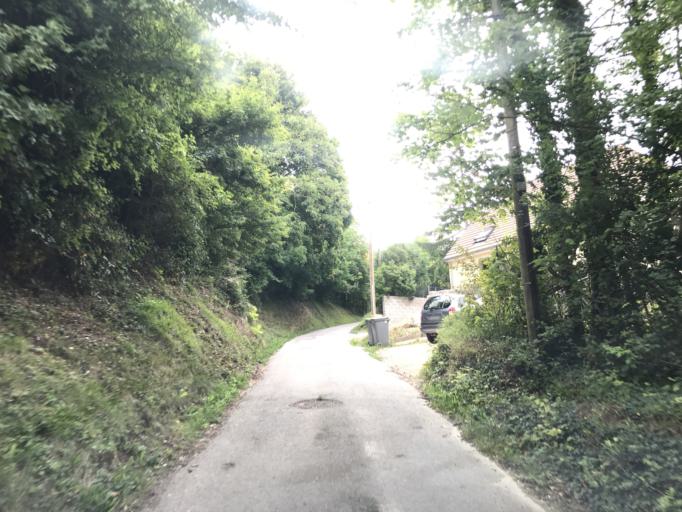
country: FR
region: Haute-Normandie
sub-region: Departement de l'Eure
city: Vernon
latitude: 49.0790
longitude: 1.4655
